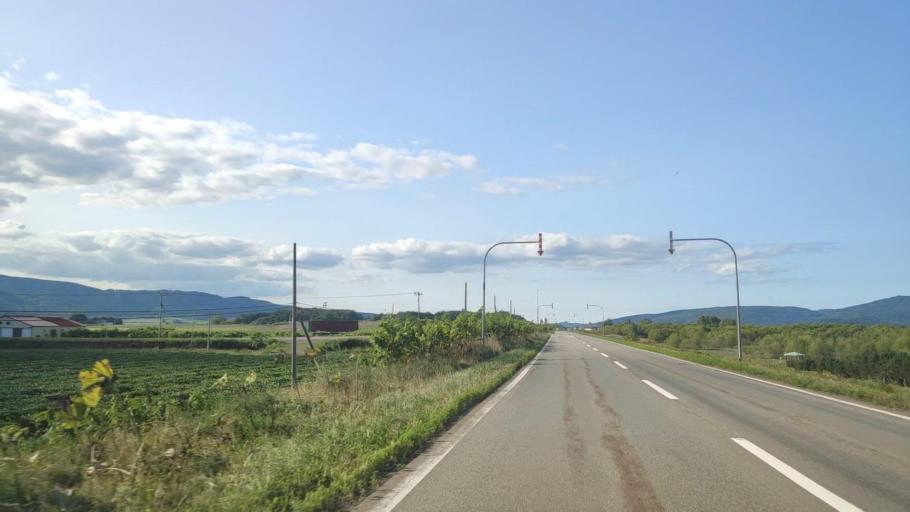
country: JP
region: Hokkaido
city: Nayoro
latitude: 44.8061
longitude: 142.0671
